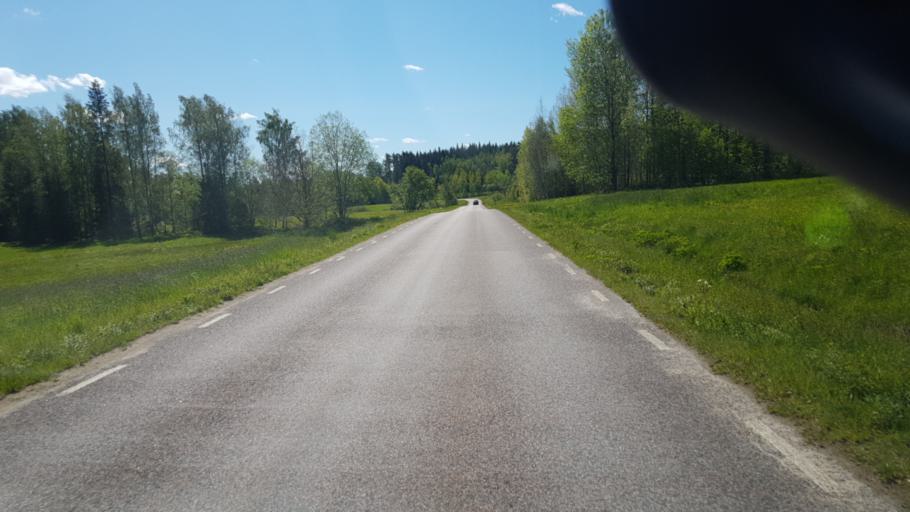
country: SE
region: Vaermland
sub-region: Grums Kommun
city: Slottsbron
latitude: 59.4642
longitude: 12.8761
